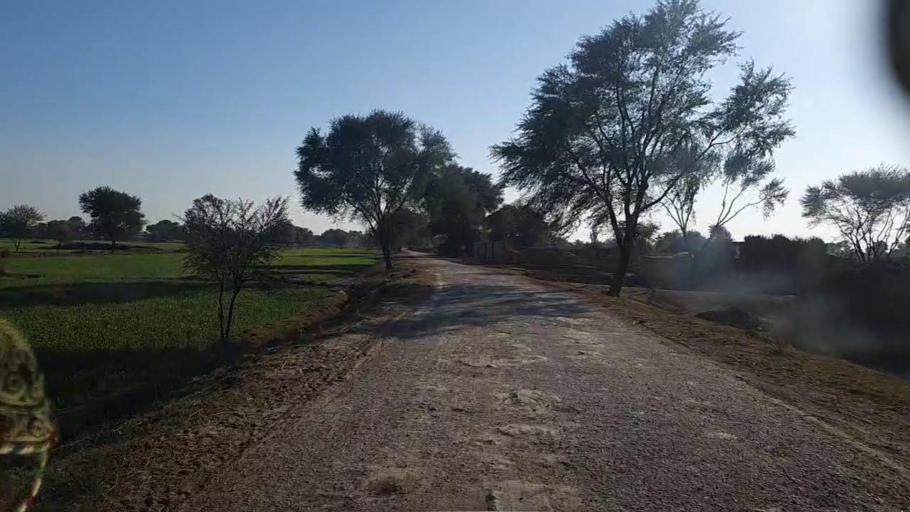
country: PK
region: Sindh
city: Khairpur
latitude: 28.0045
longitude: 69.7198
